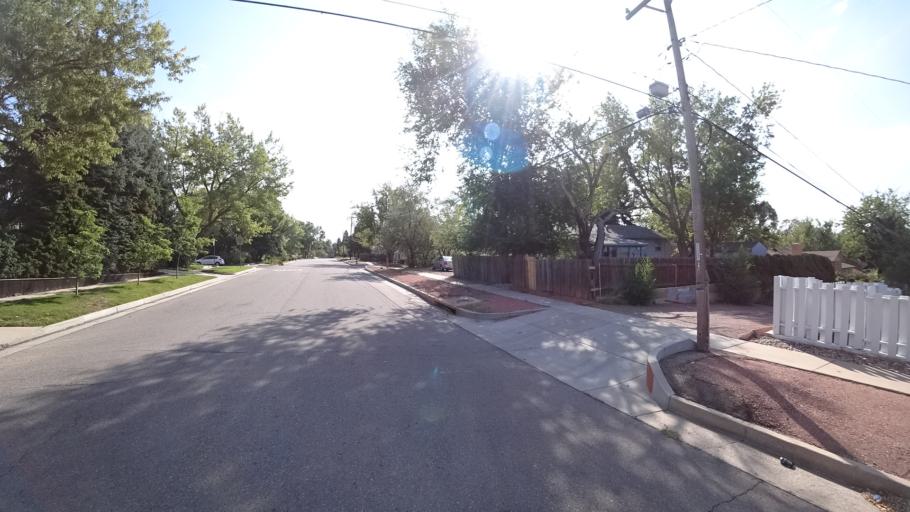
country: US
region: Colorado
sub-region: El Paso County
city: Colorado Springs
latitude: 38.8569
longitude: -104.7798
